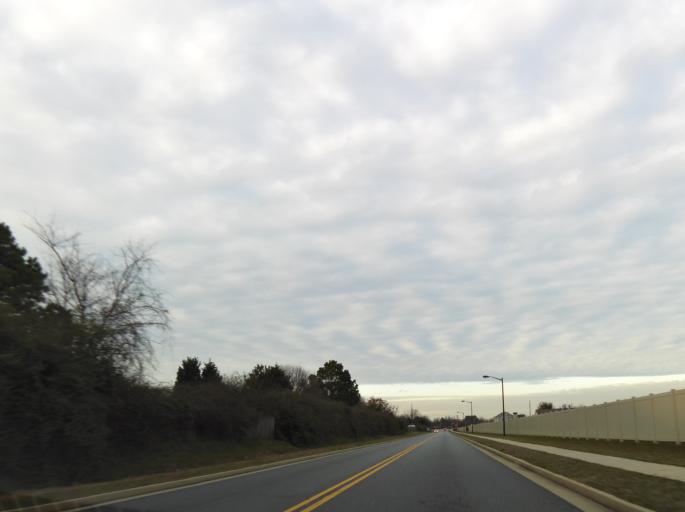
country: US
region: Georgia
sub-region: Houston County
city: Centerville
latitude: 32.6205
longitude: -83.6967
